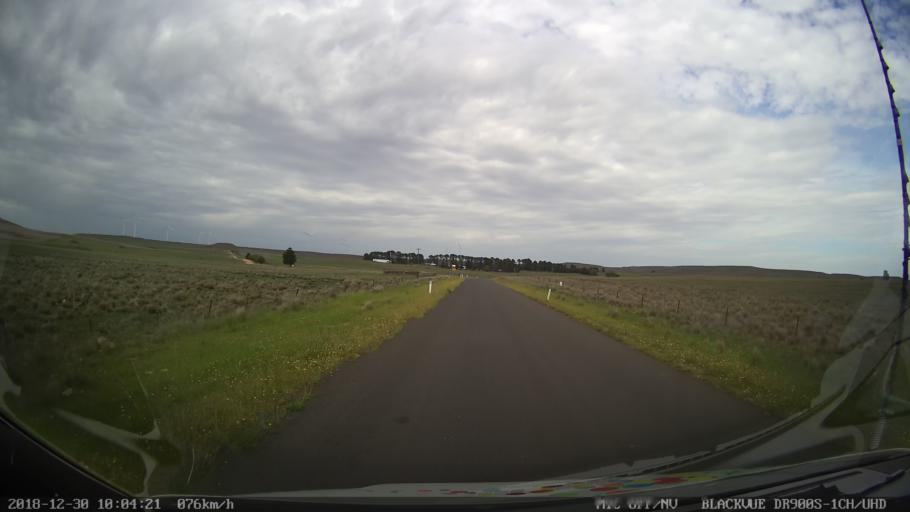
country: AU
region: New South Wales
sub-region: Cooma-Monaro
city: Cooma
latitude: -36.5211
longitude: 149.1471
